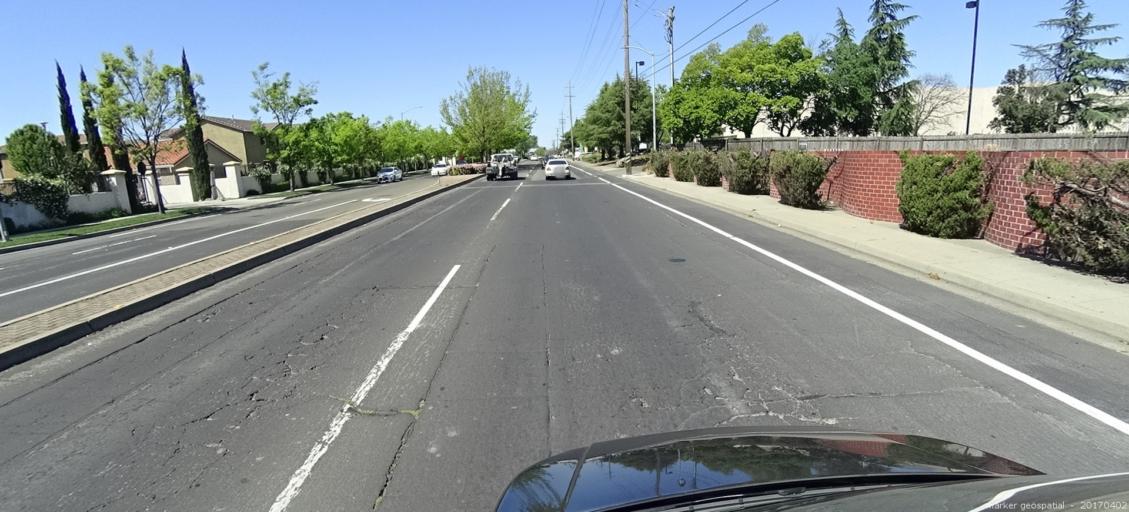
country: US
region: California
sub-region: Sacramento County
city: Parkway
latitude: 38.4713
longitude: -121.4491
